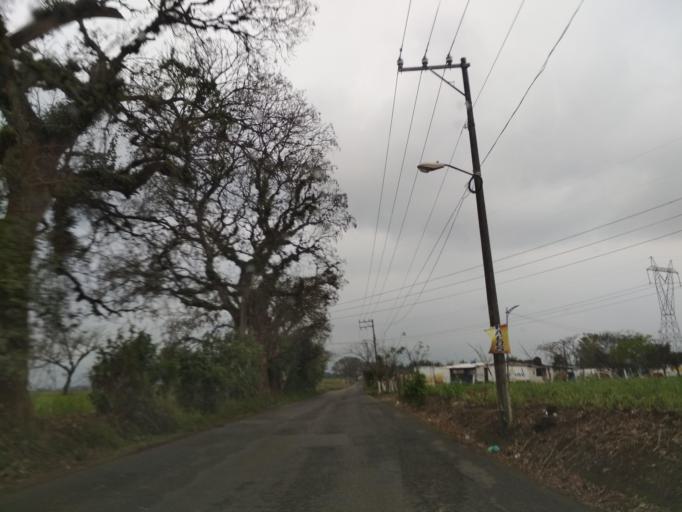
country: MX
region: Veracruz
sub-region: Cordoba
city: Veinte de Noviembre
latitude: 18.8579
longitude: -96.9513
